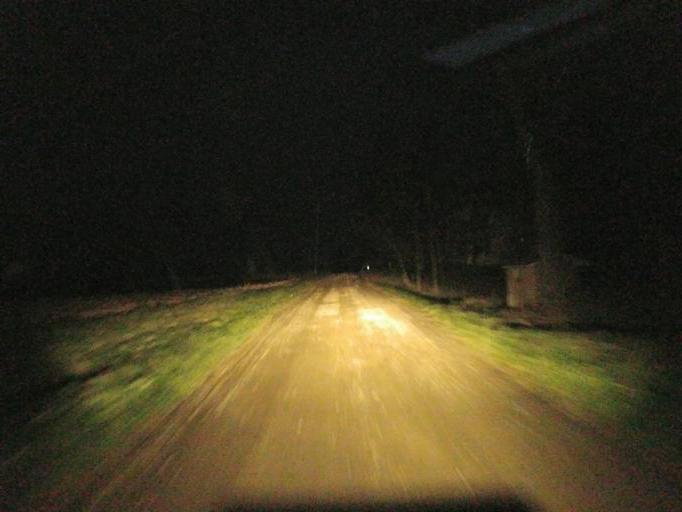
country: US
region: Ohio
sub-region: Richland County
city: Lexington
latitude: 40.5829
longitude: -82.6759
